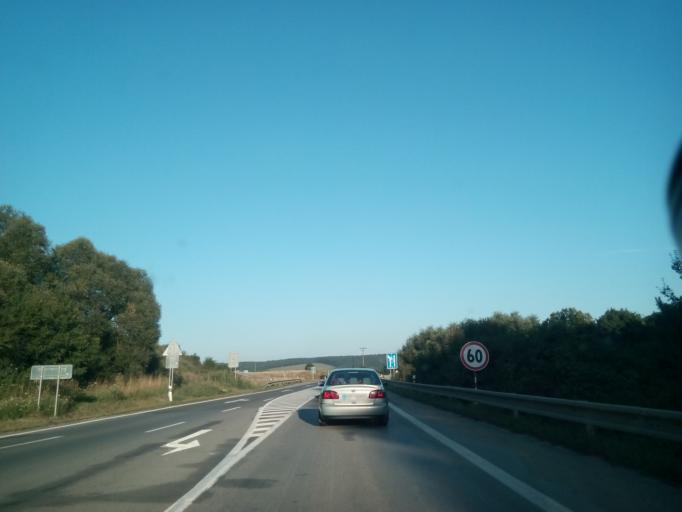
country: SK
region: Presovsky
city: Sabinov
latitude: 49.0034
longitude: 21.1012
